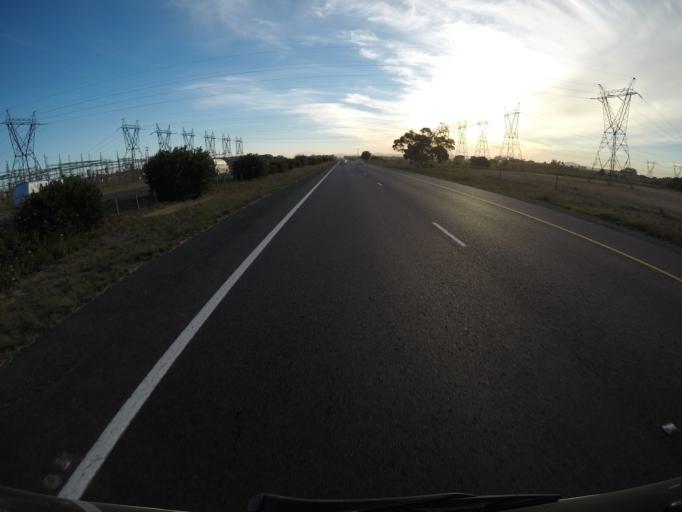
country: ZA
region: Western Cape
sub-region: City of Cape Town
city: Kraaifontein
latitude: -33.8158
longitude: 18.8057
